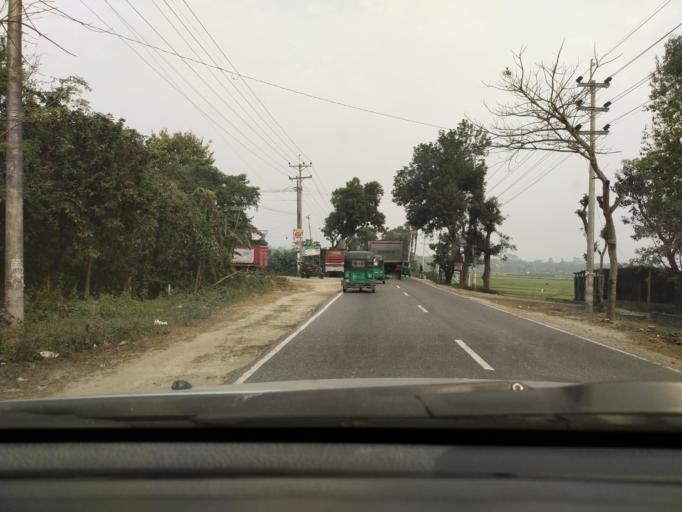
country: BD
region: Dhaka
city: Narsingdi
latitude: 24.0158
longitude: 90.7373
